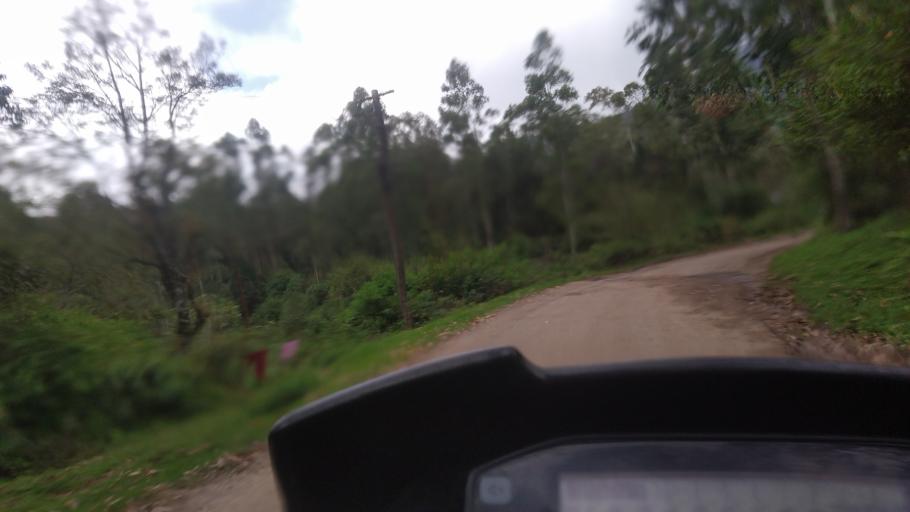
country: IN
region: Kerala
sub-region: Idukki
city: Munnar
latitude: 10.0567
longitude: 77.1089
